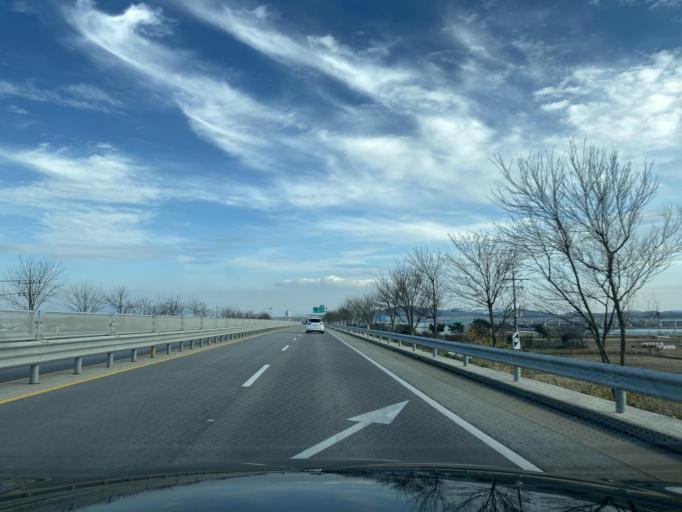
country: KR
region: Chungcheongnam-do
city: Hongsung
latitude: 36.6891
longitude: 126.7113
